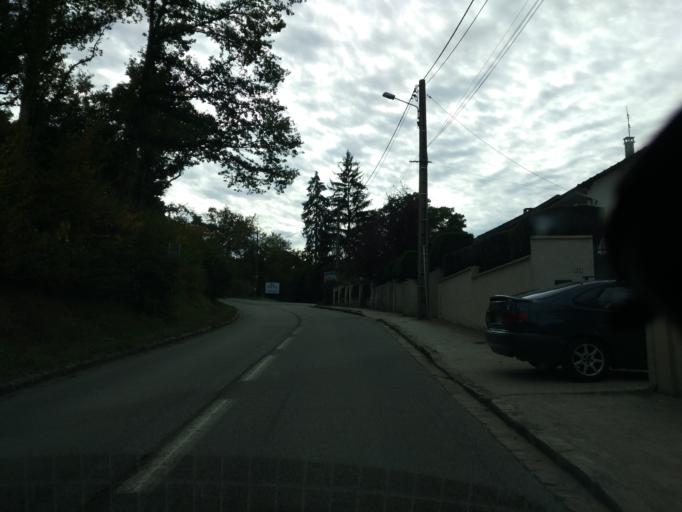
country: FR
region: Ile-de-France
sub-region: Departement des Yvelines
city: Saint-Remy-les-Chevreuse
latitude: 48.6949
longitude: 2.0672
